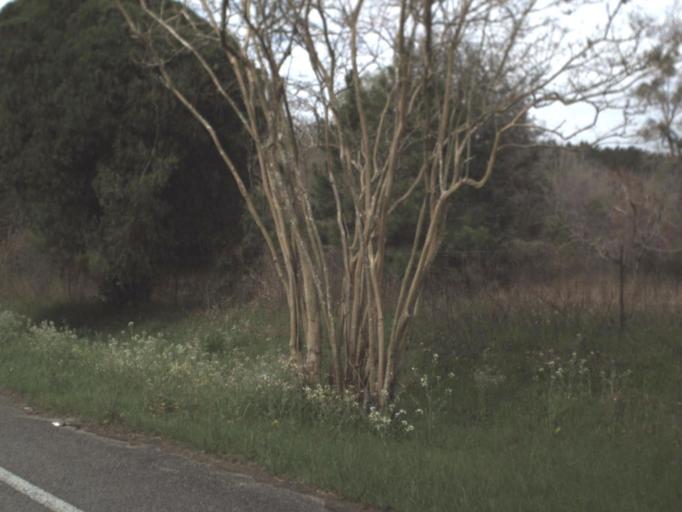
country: US
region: Florida
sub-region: Leon County
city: Tallahassee
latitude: 30.4960
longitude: -84.1062
